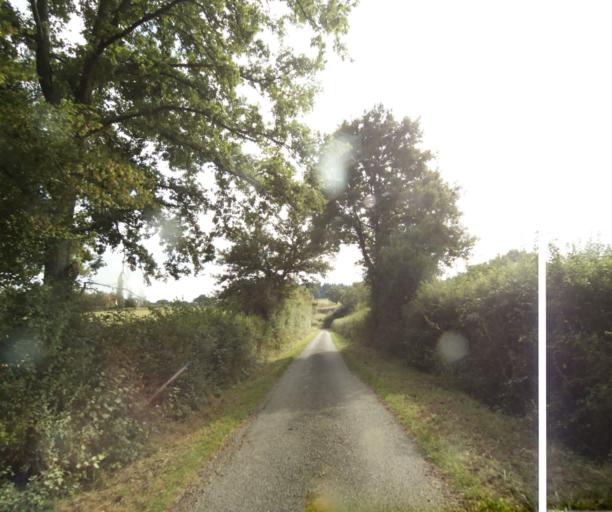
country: FR
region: Bourgogne
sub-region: Departement de Saone-et-Loire
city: Palinges
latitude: 46.5135
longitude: 4.2444
